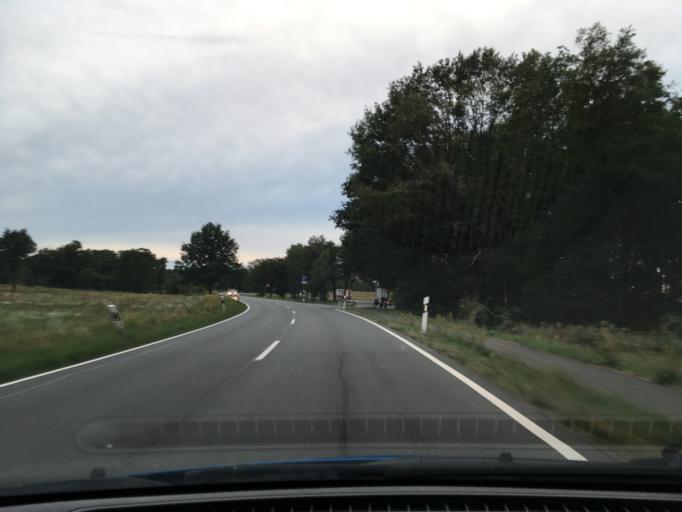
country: DE
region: Schleswig-Holstein
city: Schnakenbek
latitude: 53.3664
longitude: 10.5208
